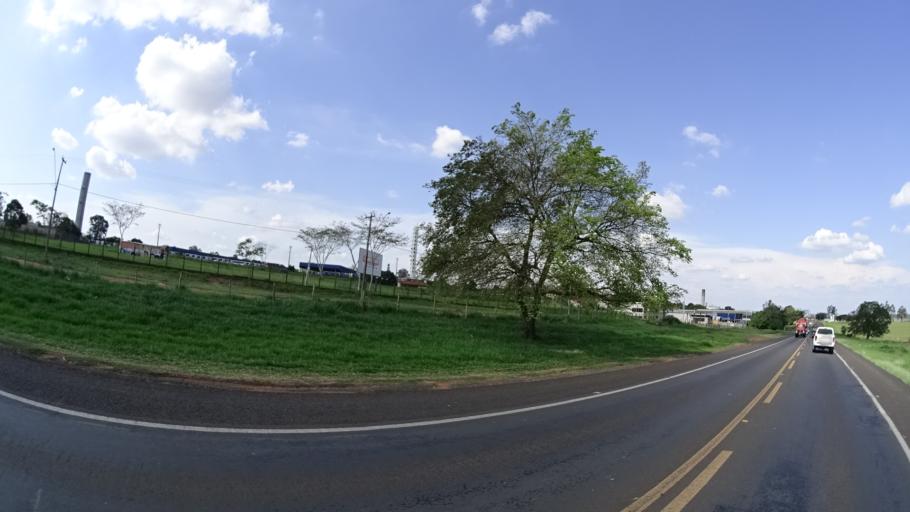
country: BR
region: Sao Paulo
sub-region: Sao Jose Do Rio Preto
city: Sao Jose do Rio Preto
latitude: -20.8507
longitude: -49.3886
